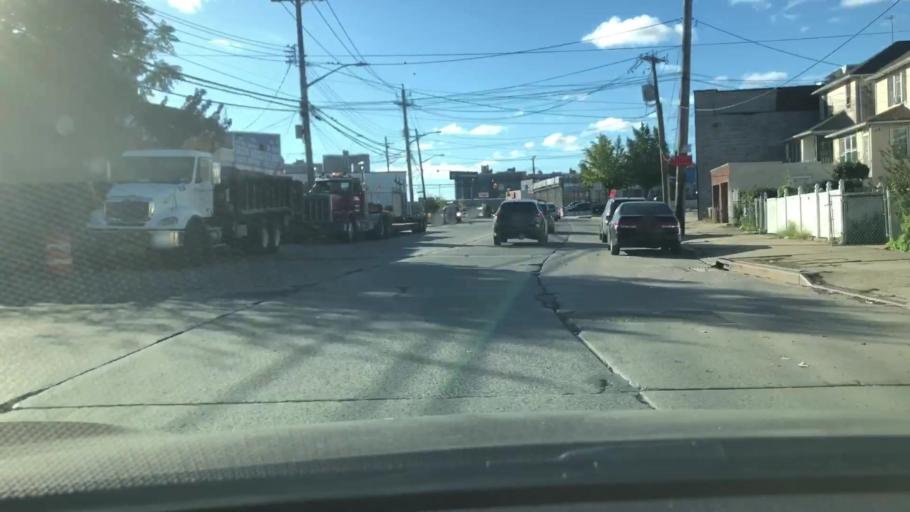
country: US
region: New York
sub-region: Bronx
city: Eastchester
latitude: 40.8873
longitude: -73.8283
